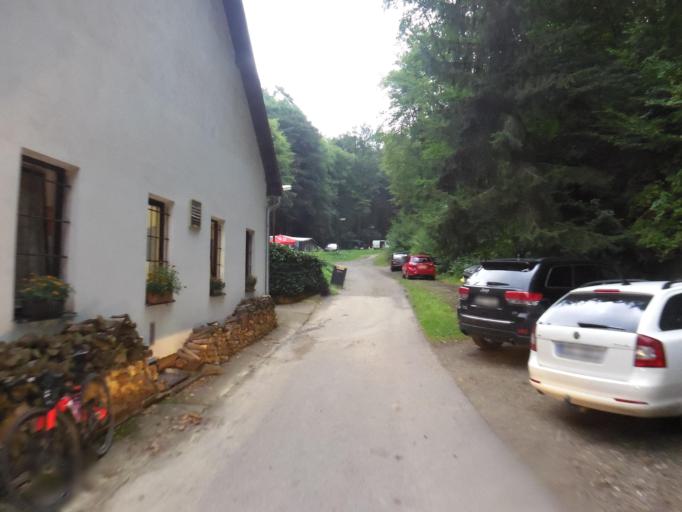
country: CZ
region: Central Bohemia
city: Mseno
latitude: 50.4382
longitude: 14.5873
